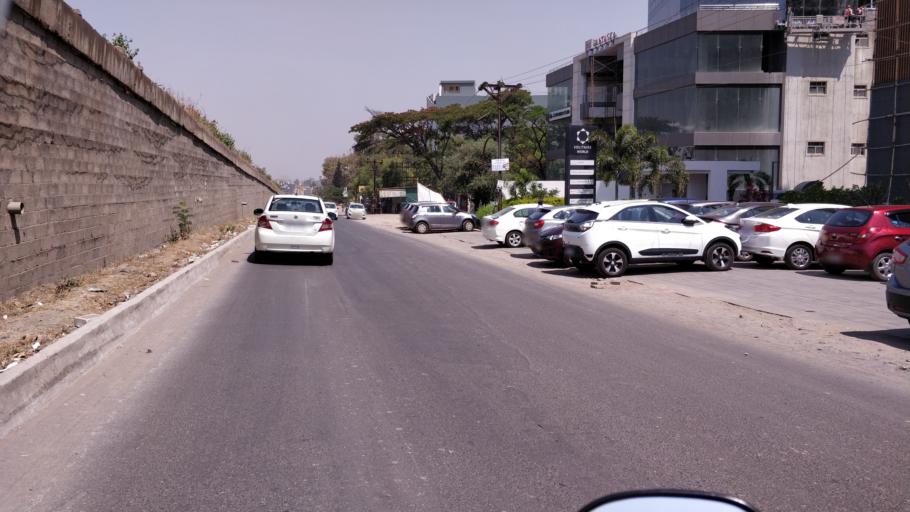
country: IN
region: Maharashtra
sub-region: Pune Division
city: Pimpri
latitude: 18.5535
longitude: 73.7716
